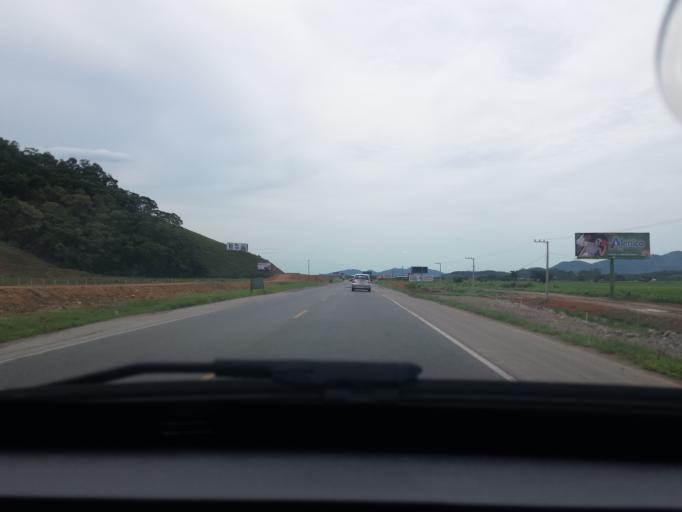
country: BR
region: Santa Catarina
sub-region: Gaspar
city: Gaspar
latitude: -26.8937
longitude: -48.9011
